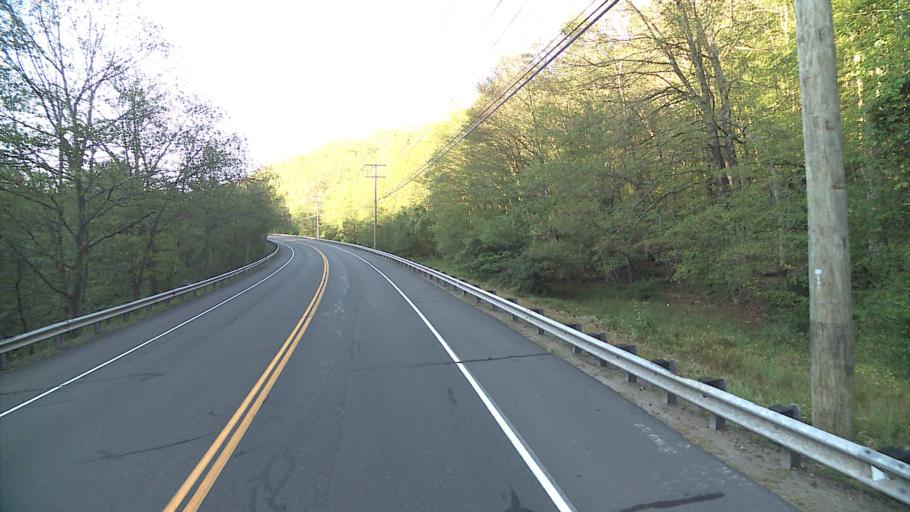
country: US
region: Connecticut
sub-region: Tolland County
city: Stafford Springs
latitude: 41.9326
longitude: -72.3097
